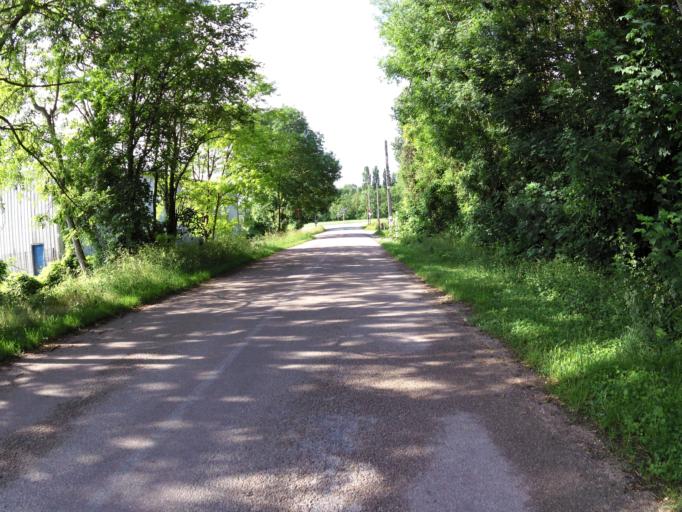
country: FR
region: Champagne-Ardenne
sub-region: Departement de l'Aube
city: Saint-Julien-les-Villas
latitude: 48.2703
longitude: 4.1103
